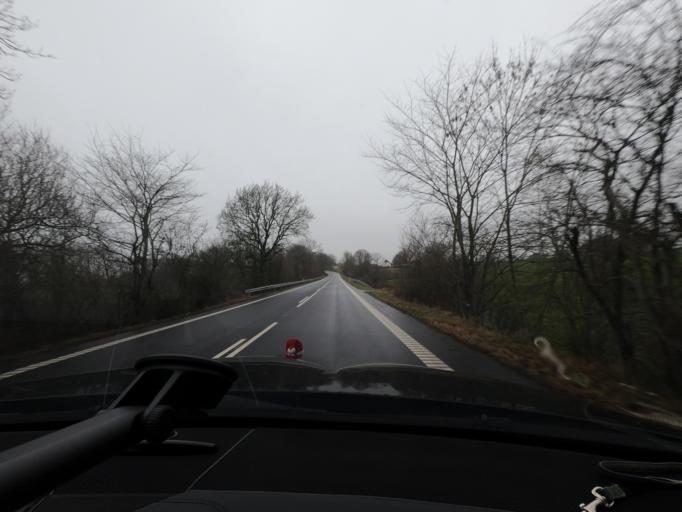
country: DE
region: Schleswig-Holstein
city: Glucksburg
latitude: 54.8874
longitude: 9.5381
